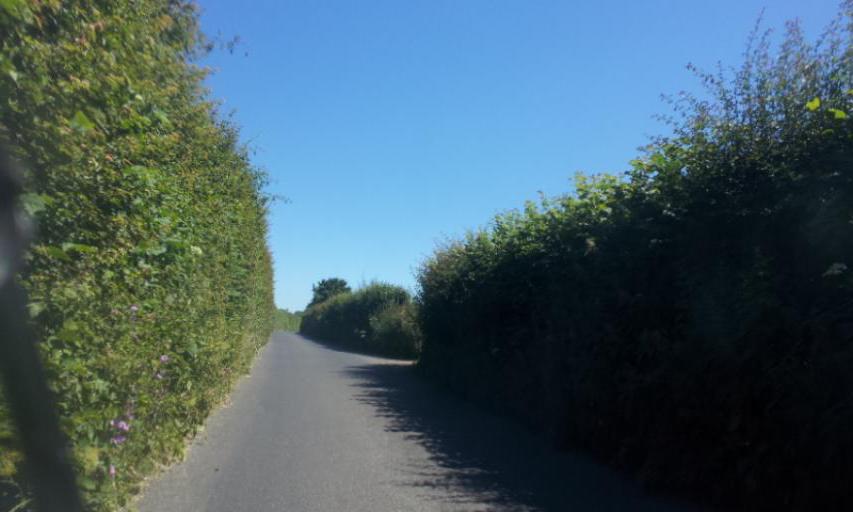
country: GB
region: England
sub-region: Kent
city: Sittingbourne
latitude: 51.3070
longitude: 0.7082
